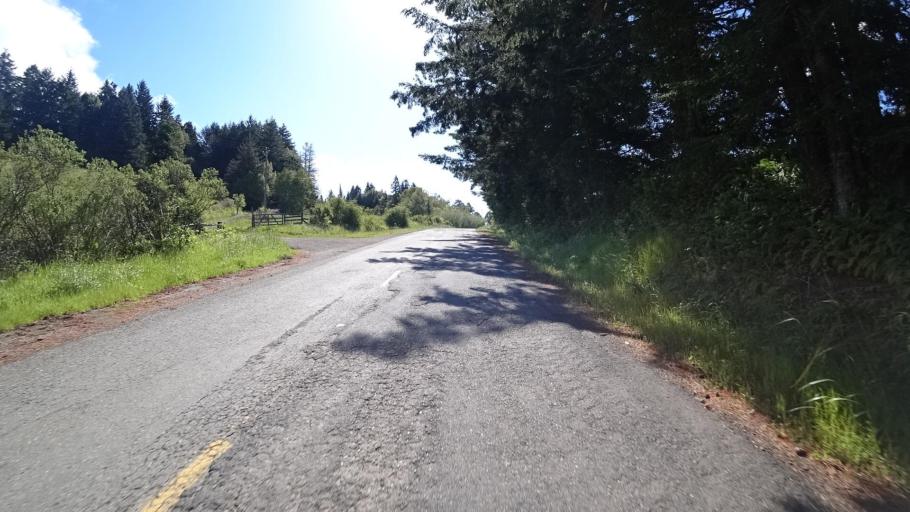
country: US
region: California
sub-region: Humboldt County
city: Ferndale
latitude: 40.3419
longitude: -124.3187
